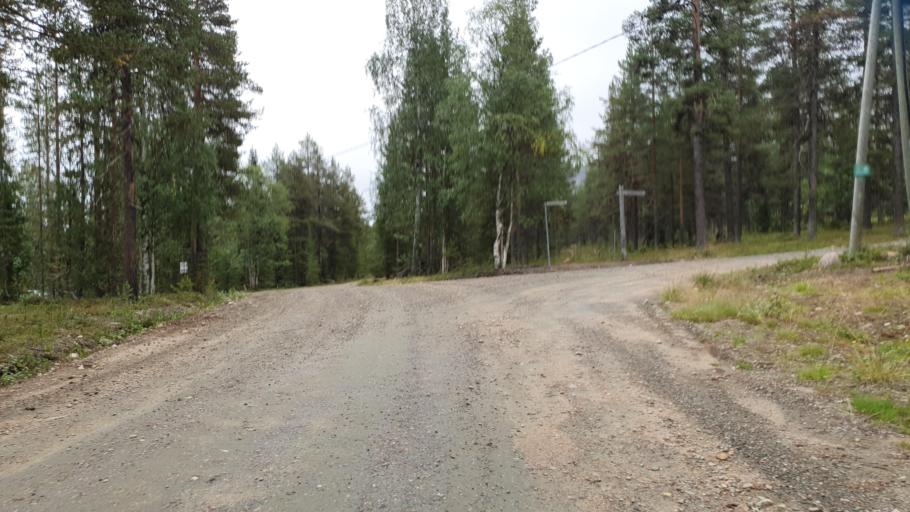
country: FI
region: Lapland
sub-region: Tunturi-Lappi
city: Kolari
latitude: 67.6007
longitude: 24.1916
